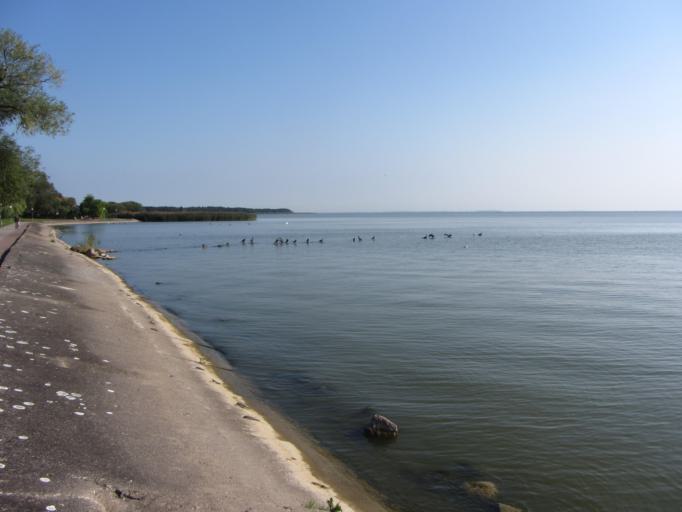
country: LT
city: Nida
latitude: 55.3119
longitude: 21.0126
